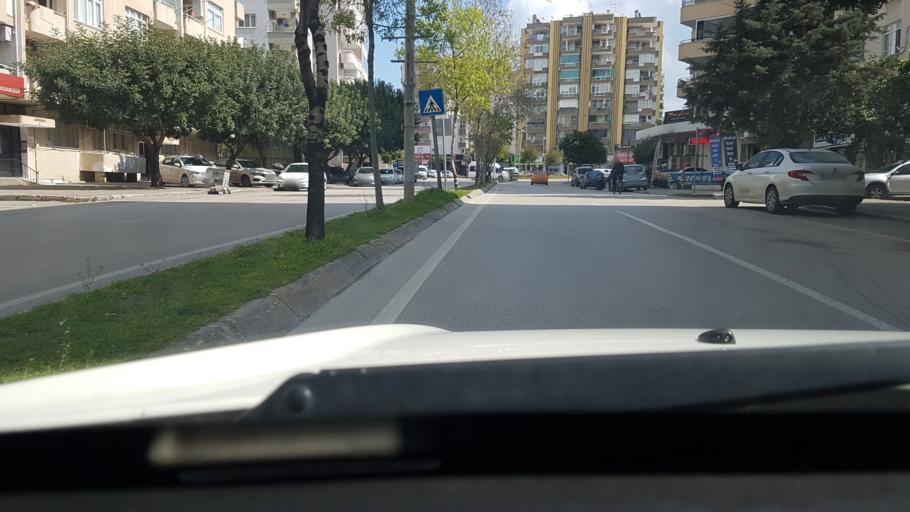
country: TR
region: Adana
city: Adana
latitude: 37.0389
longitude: 35.3013
